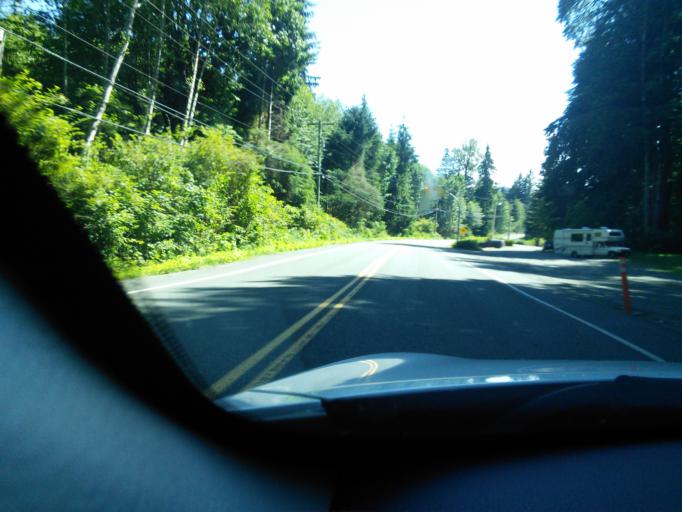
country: CA
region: British Columbia
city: Campbell River
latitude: 50.3228
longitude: -125.9221
